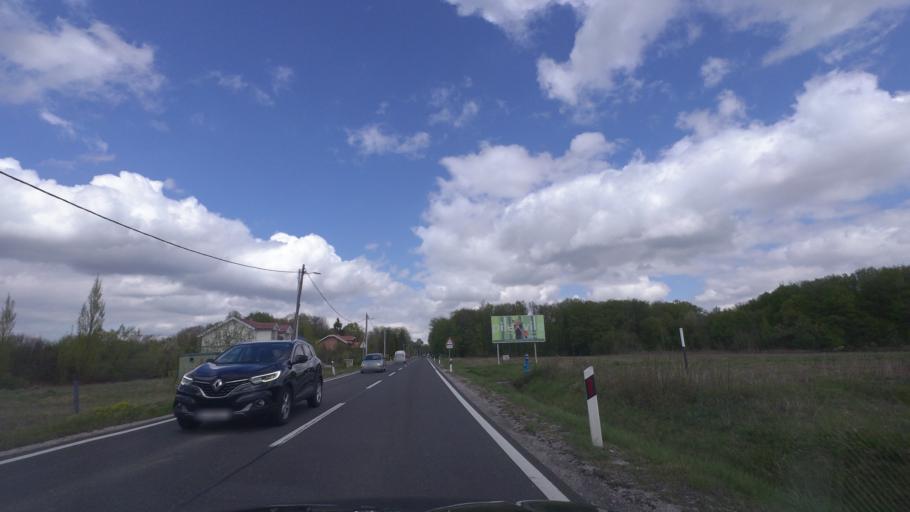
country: HR
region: Grad Zagreb
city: Horvati
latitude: 45.7164
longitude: 15.7792
